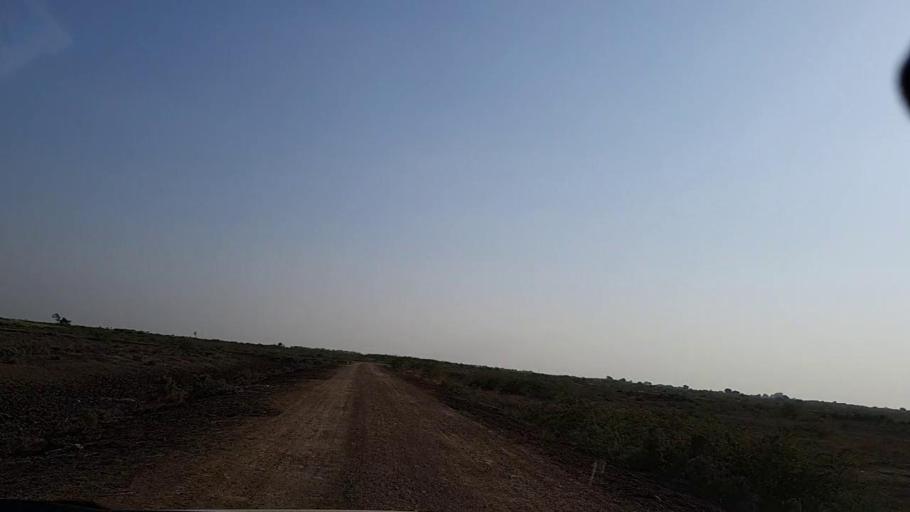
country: PK
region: Sindh
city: Mirwah Gorchani
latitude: 25.2252
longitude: 68.9731
